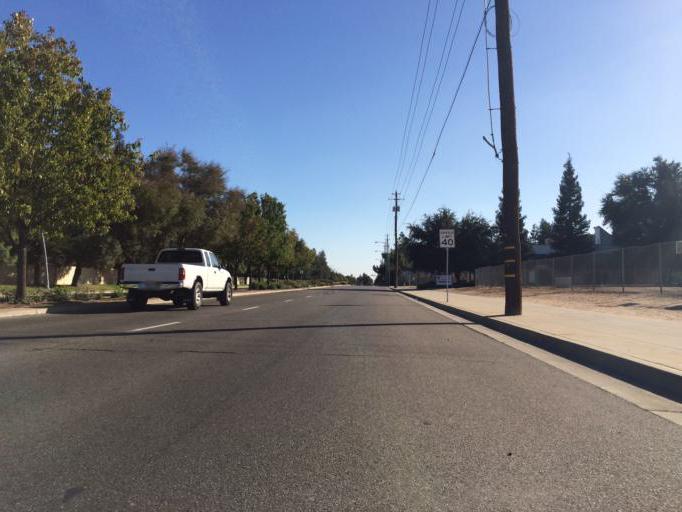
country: US
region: California
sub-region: Fresno County
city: Clovis
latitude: 36.8226
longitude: -119.6821
